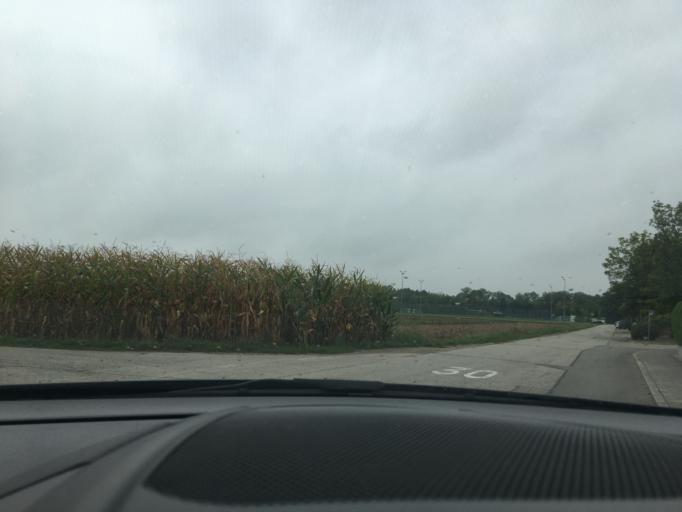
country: DE
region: Bavaria
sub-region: Upper Bavaria
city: Ismaning
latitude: 48.2547
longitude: 11.6999
